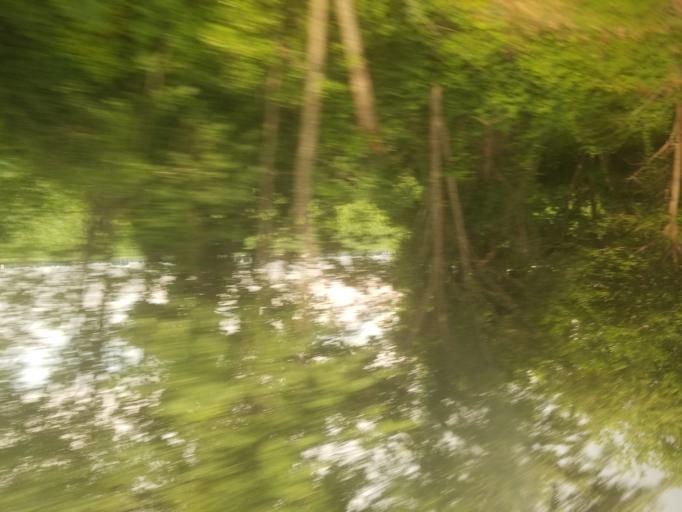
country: US
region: Illinois
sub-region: Bureau County
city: Princeton
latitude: 41.3726
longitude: -89.5603
